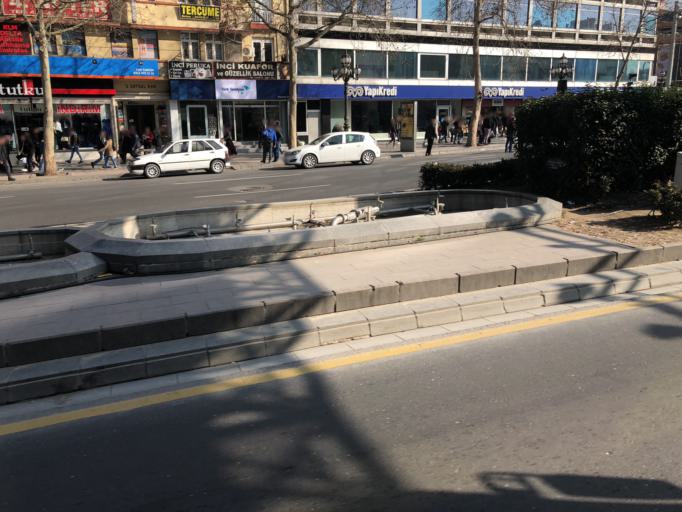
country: TR
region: Ankara
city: Ankara
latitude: 39.9208
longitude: 32.8538
